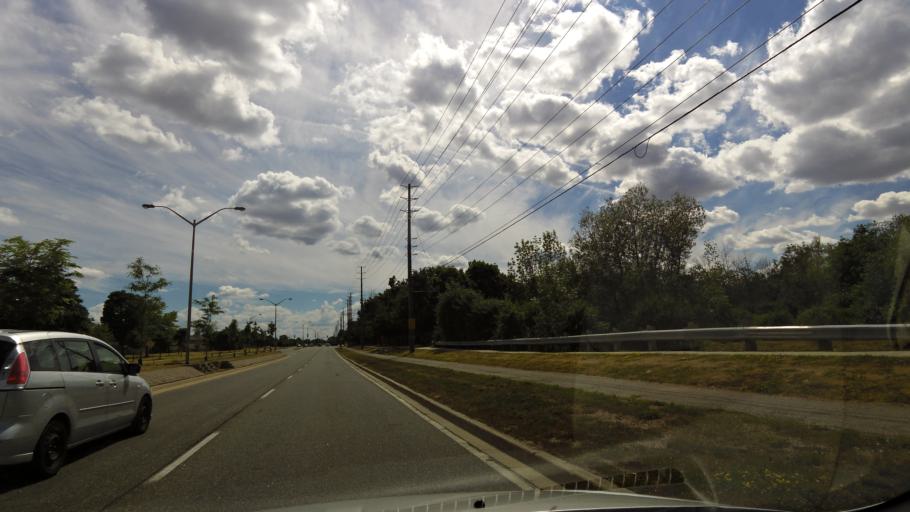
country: CA
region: Ontario
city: Oakville
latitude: 43.4685
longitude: -79.7094
